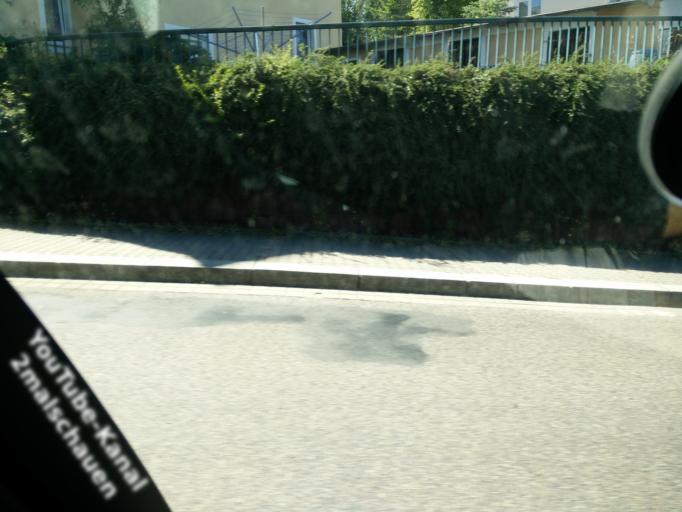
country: DE
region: Saxony
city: Waldheim
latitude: 51.0714
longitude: 13.0252
